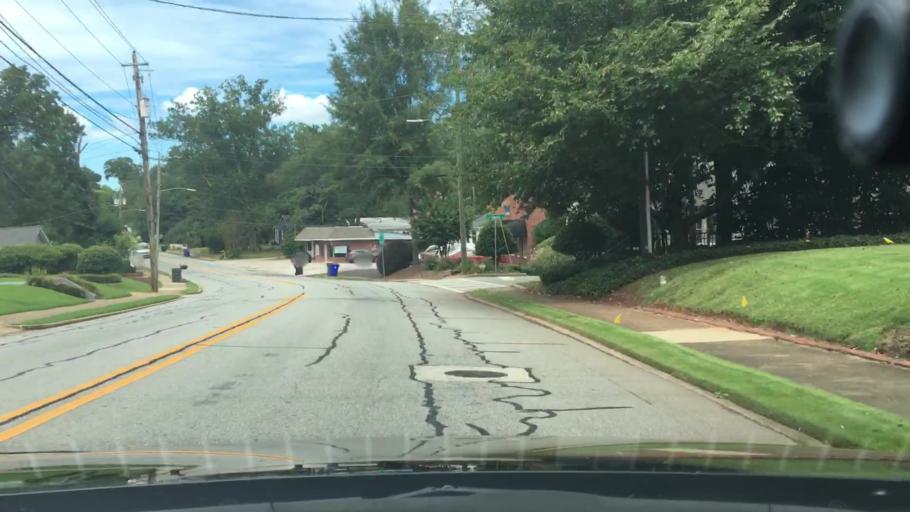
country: US
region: Georgia
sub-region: Coweta County
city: Newnan
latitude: 33.3853
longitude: -84.8000
